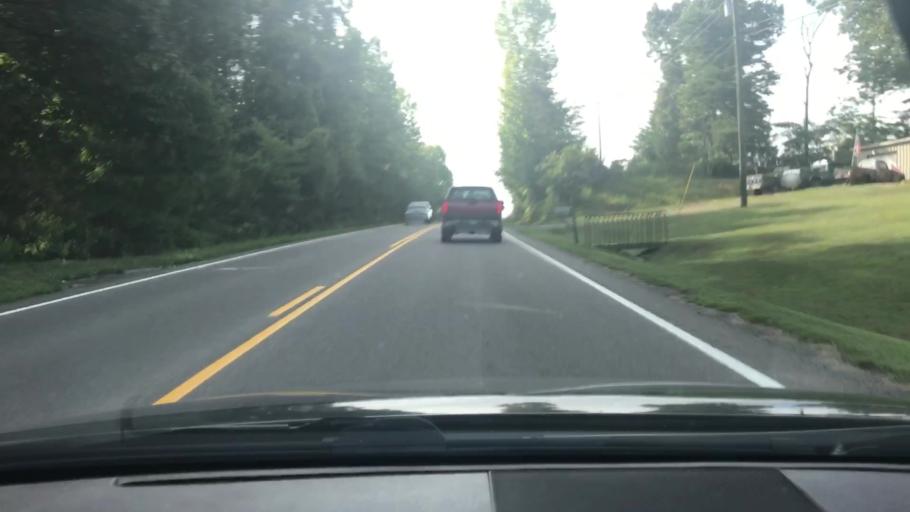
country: US
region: Tennessee
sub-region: Williamson County
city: Fairview
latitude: 36.0181
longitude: -87.1615
